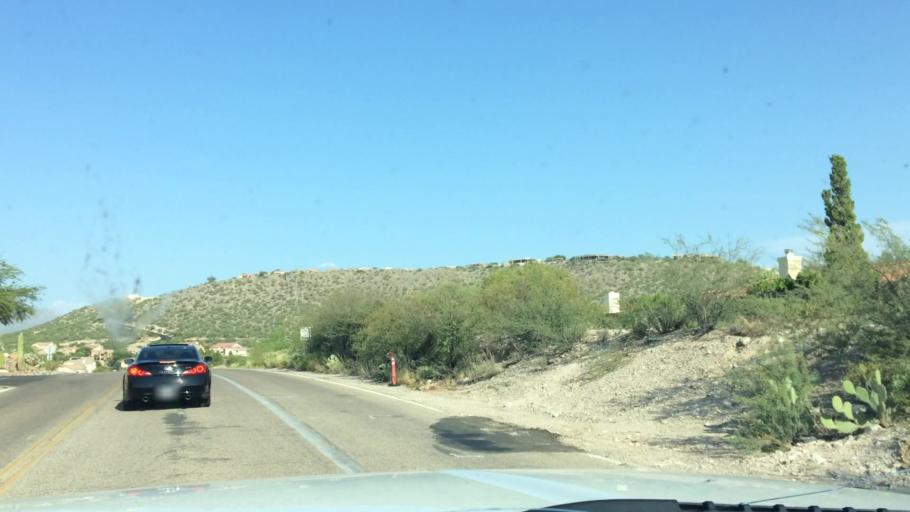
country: US
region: Arizona
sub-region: Pima County
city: Catalina Foothills
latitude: 32.2941
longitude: -110.8333
